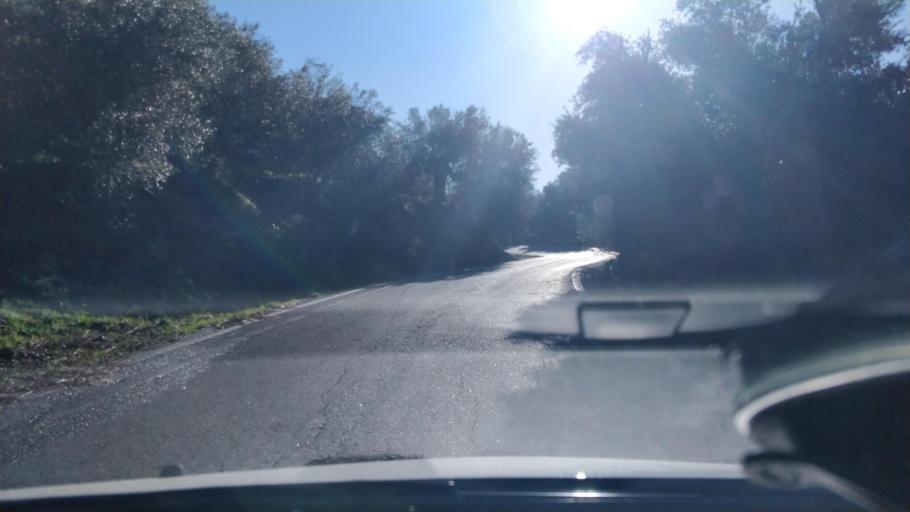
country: GR
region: Crete
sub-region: Nomos Lasithiou
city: Gra Liyia
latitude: 35.0509
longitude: 25.5801
